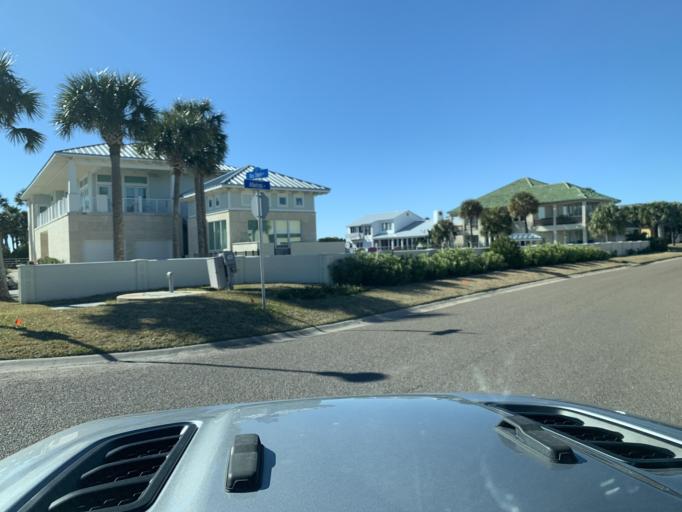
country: US
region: Texas
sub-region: Aransas County
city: Rockport
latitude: 28.0321
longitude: -97.0261
